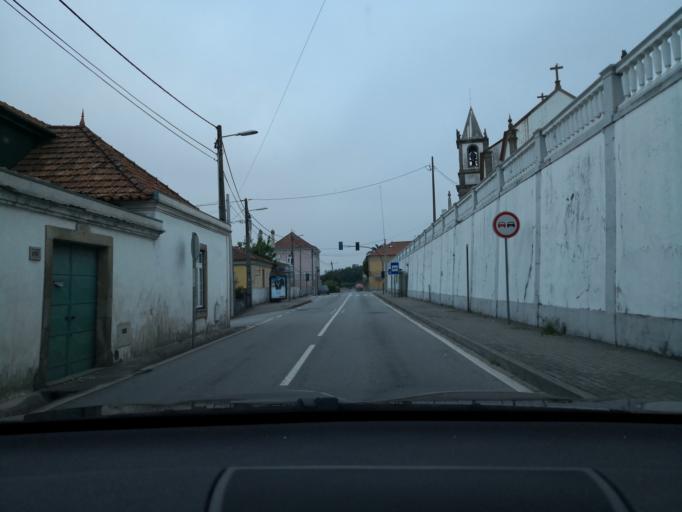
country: PT
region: Aveiro
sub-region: Santa Maria da Feira
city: Lamas
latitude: 41.0017
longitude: -8.5650
